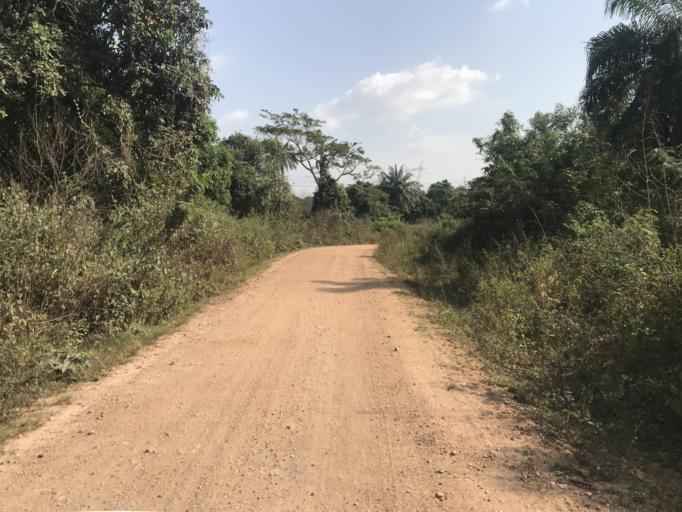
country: NG
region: Osun
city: Ikirun
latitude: 7.8753
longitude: 4.5862
